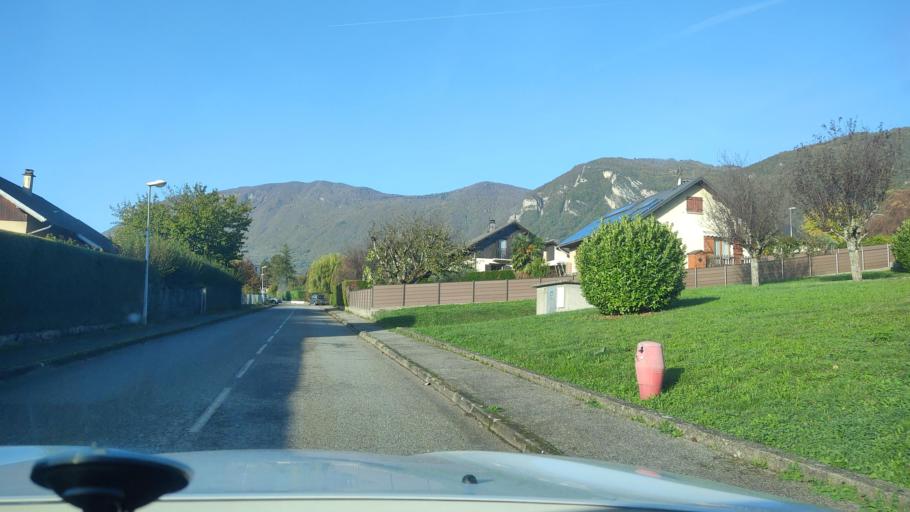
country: FR
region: Rhone-Alpes
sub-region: Departement de la Savoie
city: Coise-Saint-Jean-Pied-Gauthier
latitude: 45.5705
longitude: 6.1644
